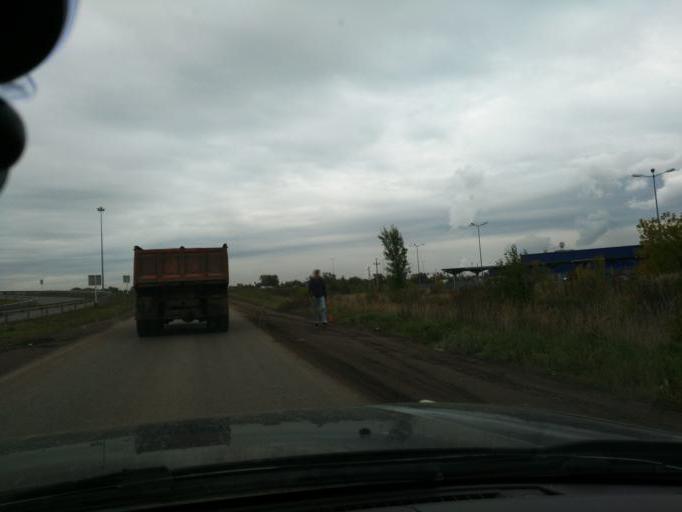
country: RU
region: Perm
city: Kondratovo
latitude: 57.9535
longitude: 56.1197
